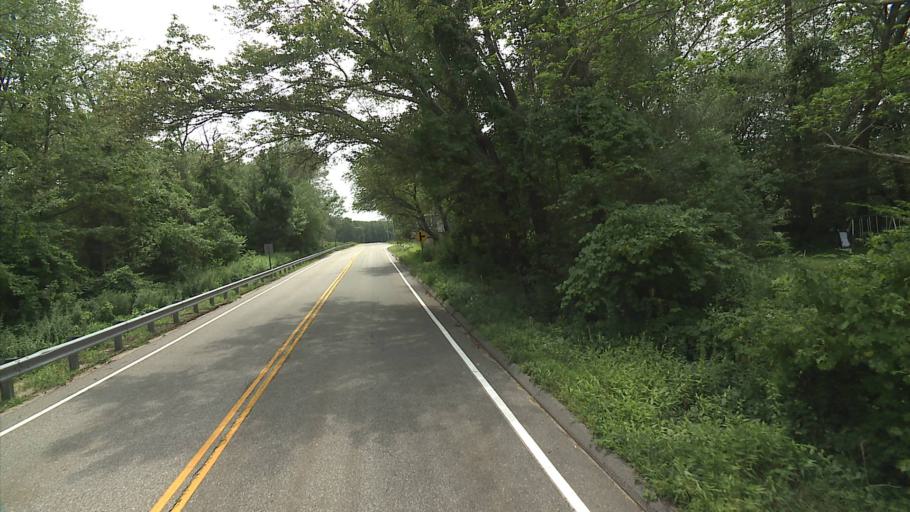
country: US
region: Connecticut
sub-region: Windham County
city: Danielson
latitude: 41.8032
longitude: -71.8733
